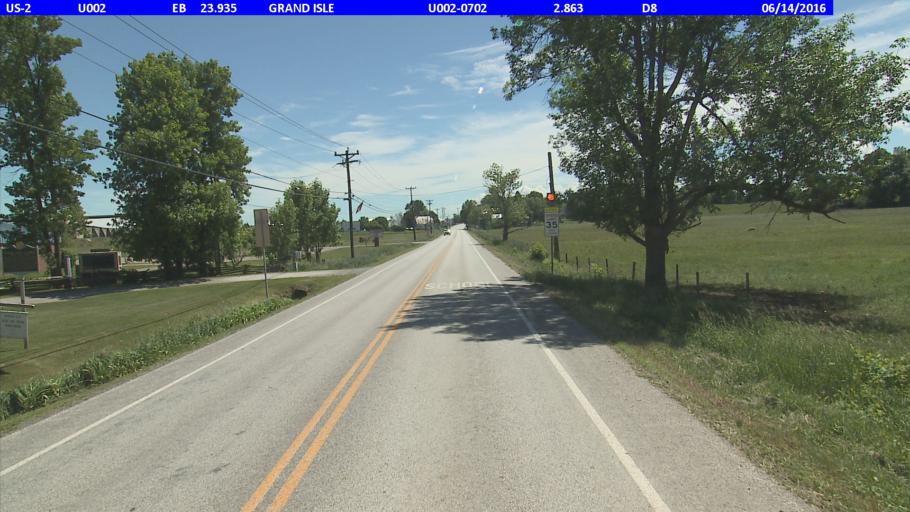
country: US
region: Vermont
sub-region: Grand Isle County
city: North Hero
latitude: 44.7263
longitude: -73.2925
